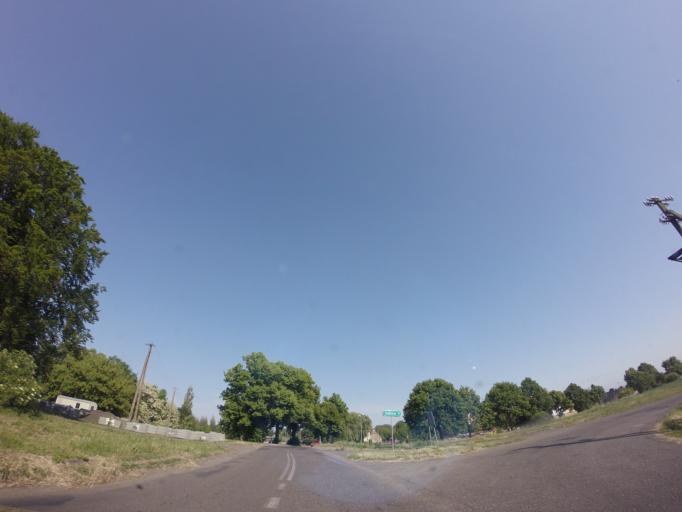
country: PL
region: West Pomeranian Voivodeship
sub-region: Powiat gryfinski
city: Stare Czarnowo
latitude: 53.3029
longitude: 14.8093
